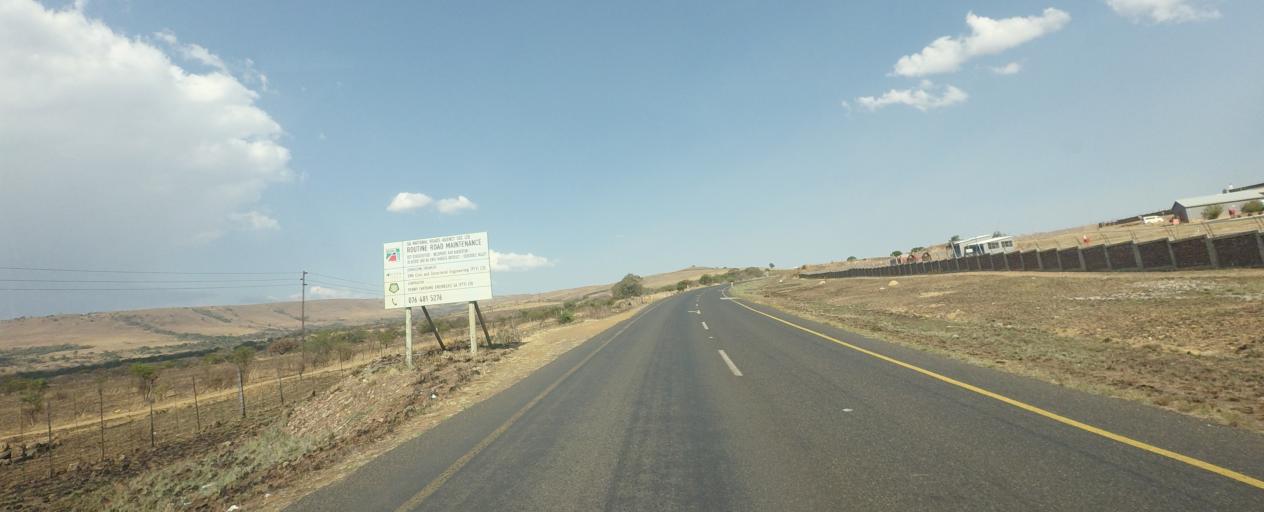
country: ZA
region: Mpumalanga
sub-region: Ehlanzeni District
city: Lydenburg
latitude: -25.1049
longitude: 30.4882
